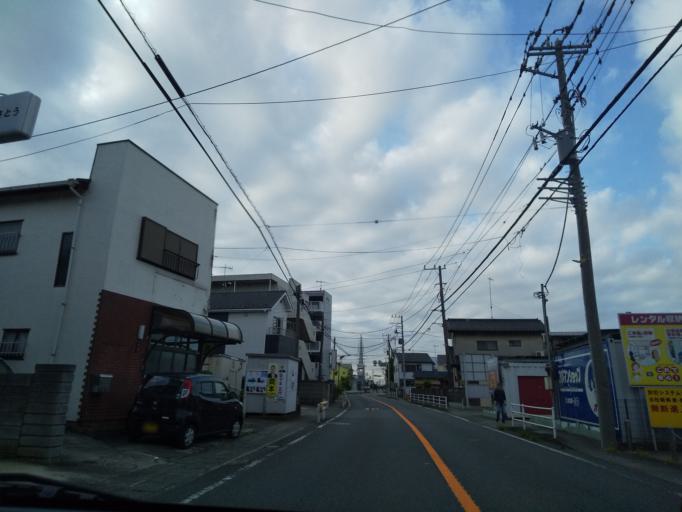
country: JP
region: Kanagawa
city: Zama
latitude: 35.5398
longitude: 139.3672
